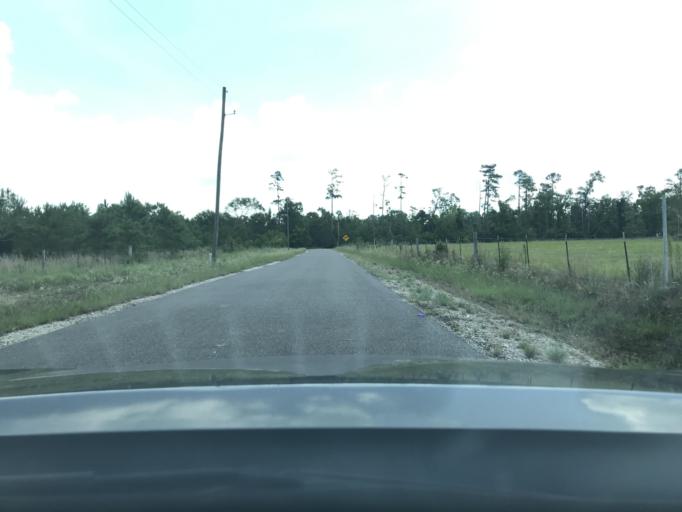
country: US
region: Louisiana
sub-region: Calcasieu Parish
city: Moss Bluff
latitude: 30.3374
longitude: -93.1281
